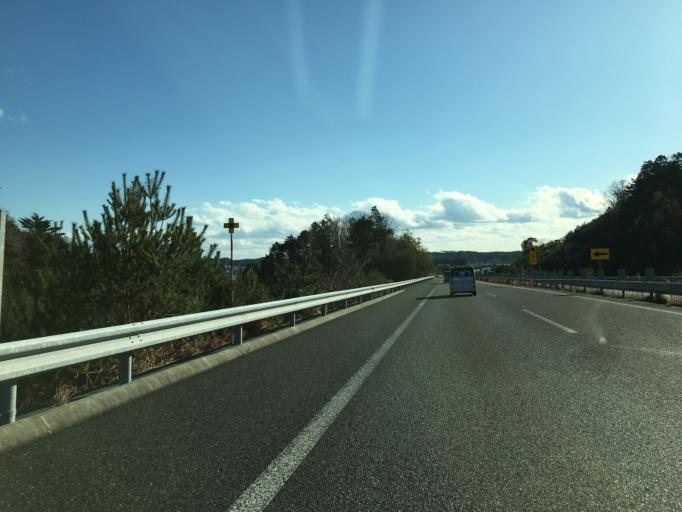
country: JP
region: Fukushima
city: Namie
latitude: 37.6721
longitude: 140.9189
